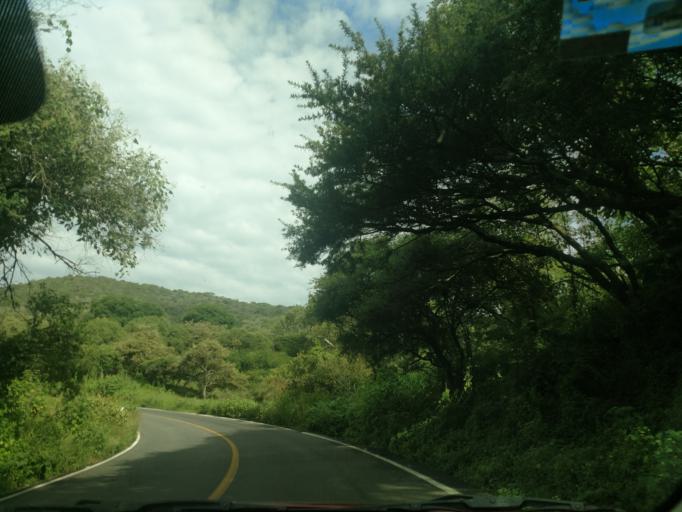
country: MX
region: Jalisco
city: Ameca
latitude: 20.5412
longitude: -104.1910
